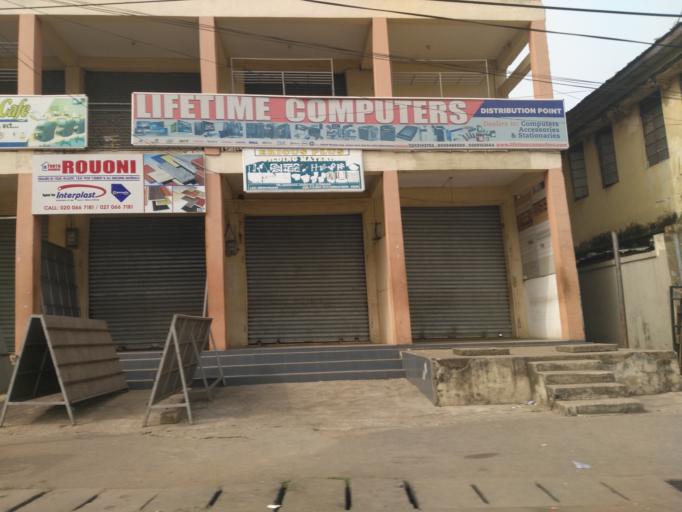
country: GH
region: Ashanti
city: Kumasi
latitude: 6.6910
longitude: -1.6198
